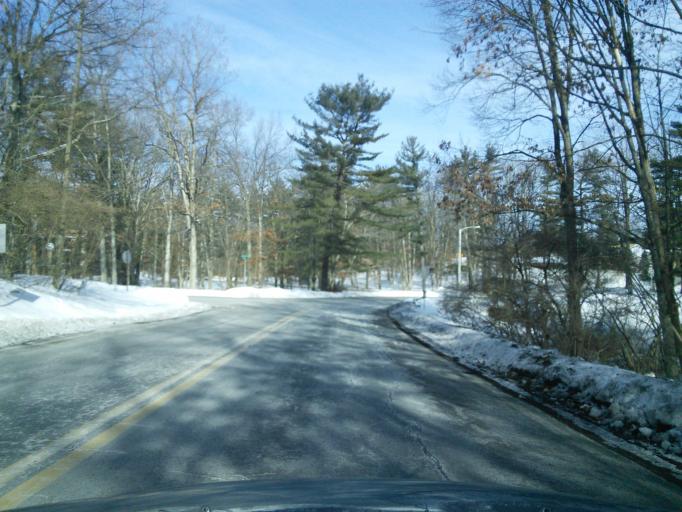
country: US
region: Pennsylvania
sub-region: Centre County
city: Park Forest Village
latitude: 40.8311
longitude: -77.8819
